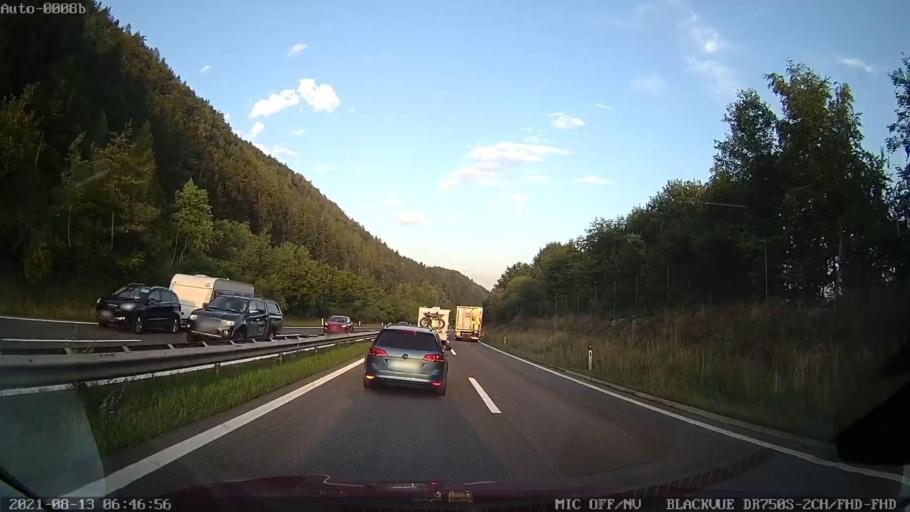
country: AT
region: Carinthia
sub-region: Politischer Bezirk Villach Land
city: Wernberg
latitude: 46.5911
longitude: 13.9695
